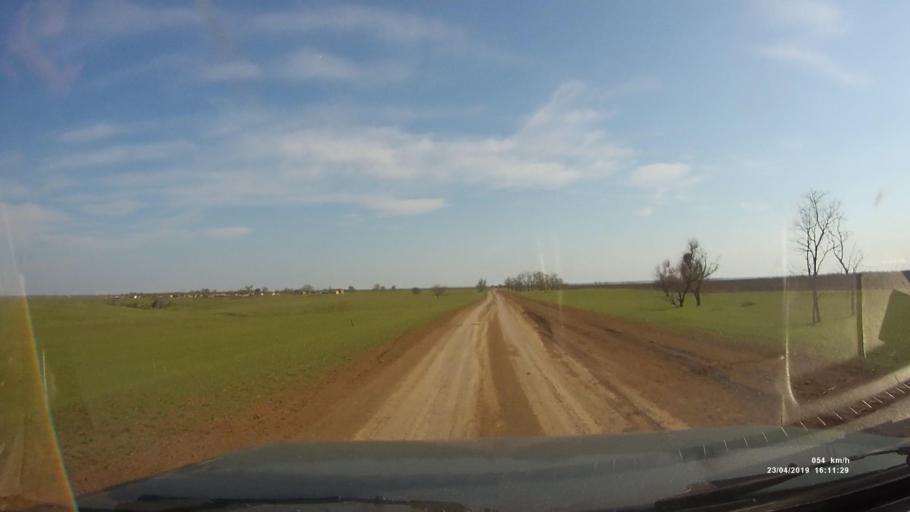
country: RU
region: Rostov
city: Remontnoye
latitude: 46.4736
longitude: 43.1231
